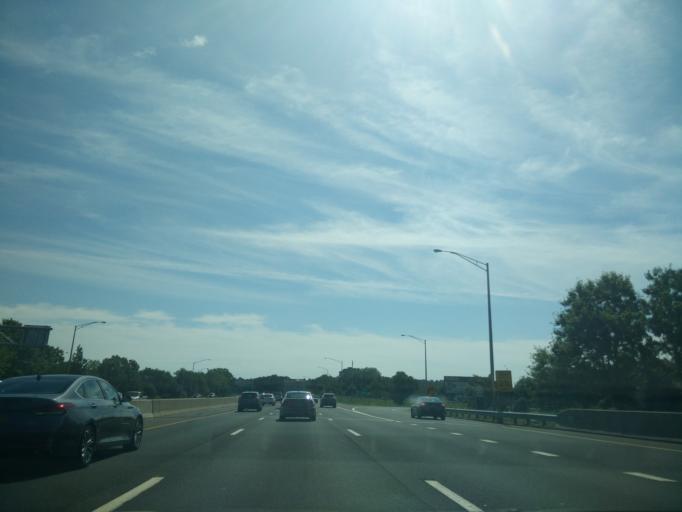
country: US
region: Connecticut
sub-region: New Haven County
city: Milford
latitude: 41.2342
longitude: -73.0420
